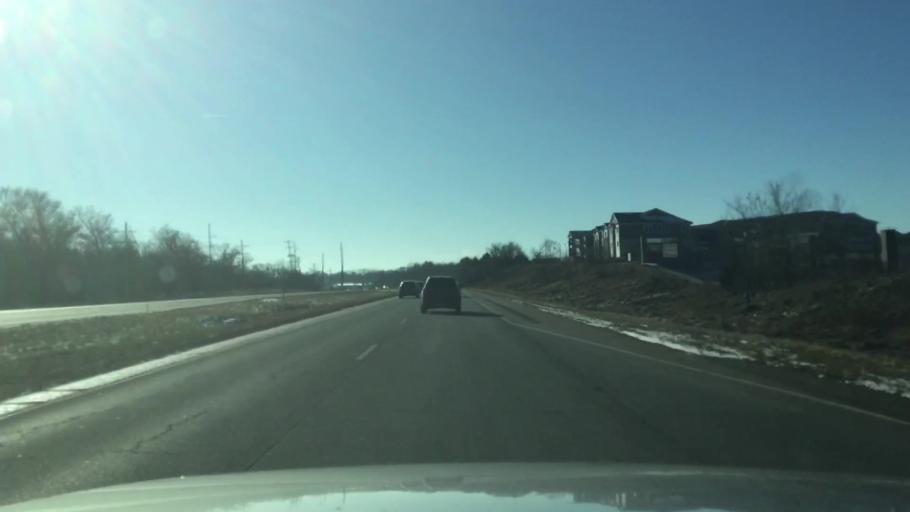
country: US
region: Wisconsin
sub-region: Racine County
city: Browns Lake
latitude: 42.7011
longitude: -88.2542
